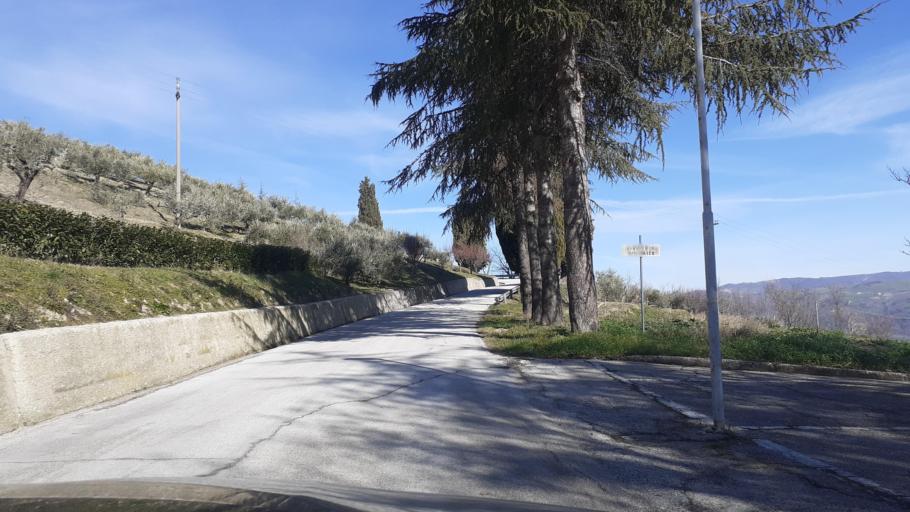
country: IT
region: Molise
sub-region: Provincia di Campobasso
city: Pietracupa
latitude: 41.6834
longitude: 14.5223
